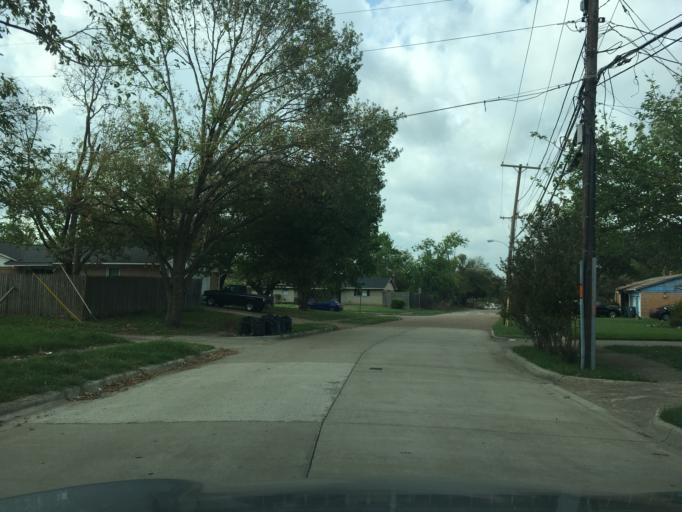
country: US
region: Texas
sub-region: Dallas County
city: Richardson
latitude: 32.9050
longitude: -96.7566
